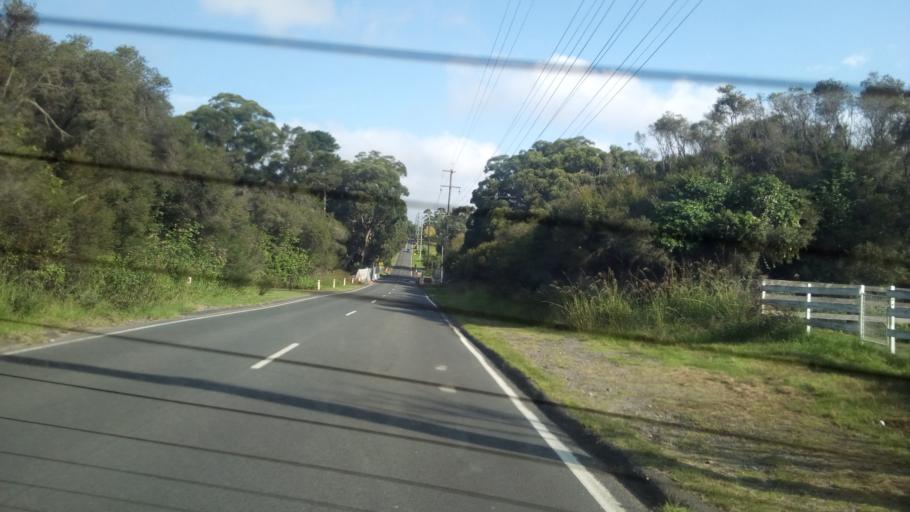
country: AU
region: New South Wales
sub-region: Wollongong
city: Helensburgh
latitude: -34.2064
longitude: 150.9787
